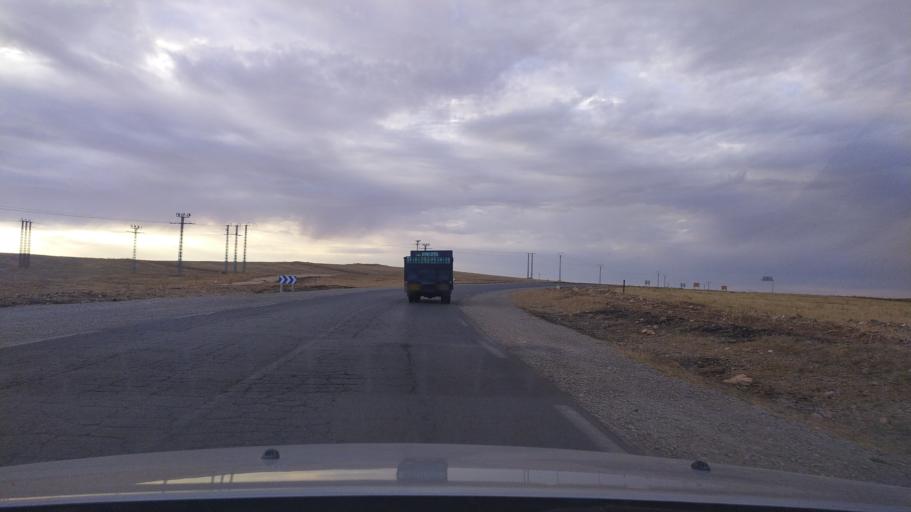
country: DZ
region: Tiaret
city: Frenda
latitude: 34.9878
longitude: 1.1328
